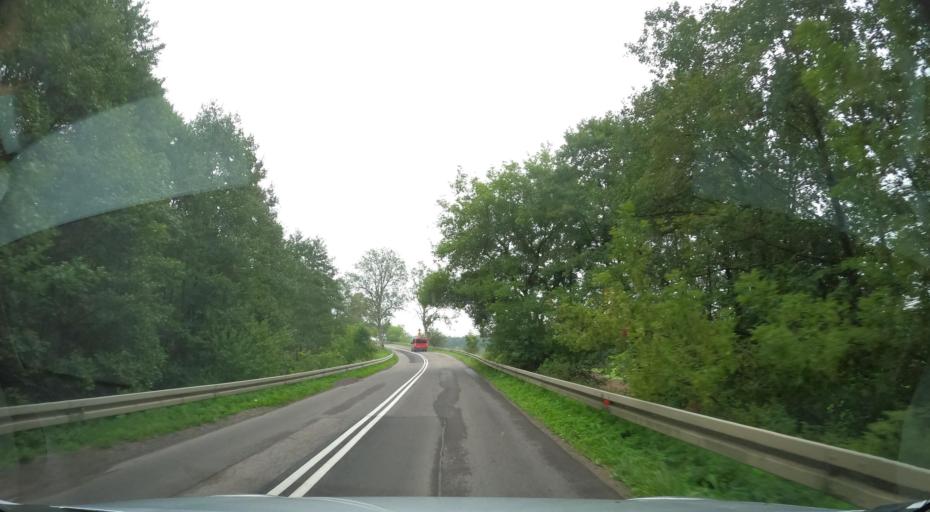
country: PL
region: Pomeranian Voivodeship
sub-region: Powiat wejherowski
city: Linia
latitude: 54.4582
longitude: 18.0020
